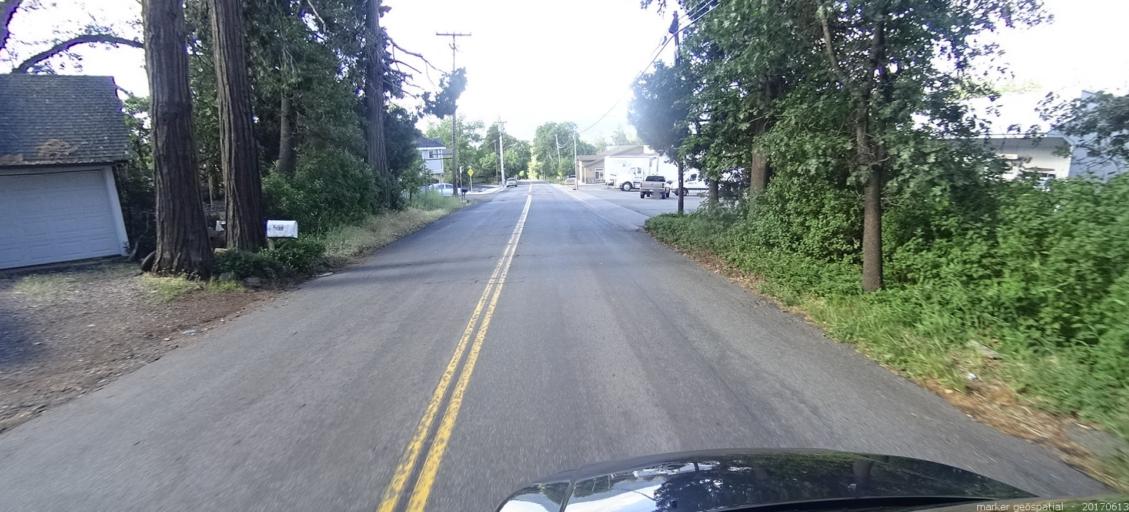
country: US
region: California
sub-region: Siskiyou County
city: Mount Shasta
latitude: 41.3043
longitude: -122.3111
